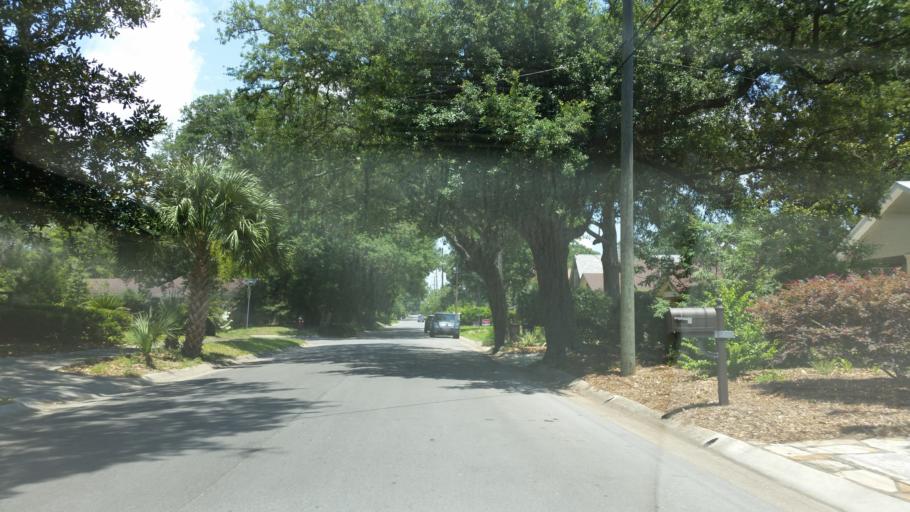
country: US
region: Florida
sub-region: Escambia County
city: East Pensacola Heights
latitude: 30.4379
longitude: -87.1920
